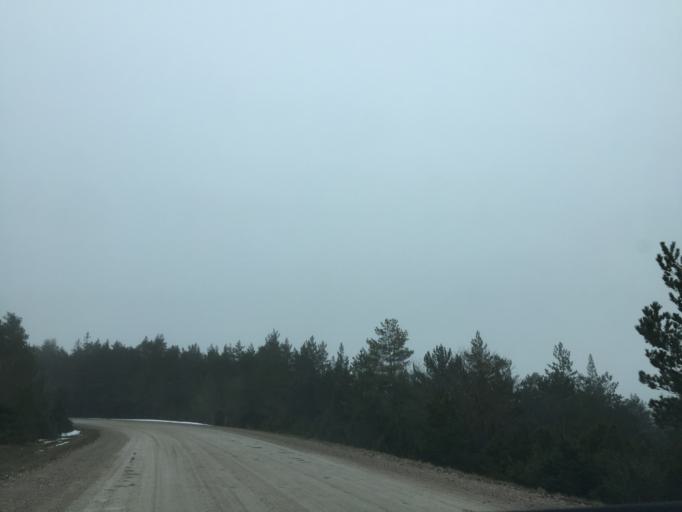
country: EE
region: Saare
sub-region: Kuressaare linn
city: Kuressaare
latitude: 58.4903
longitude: 21.9856
